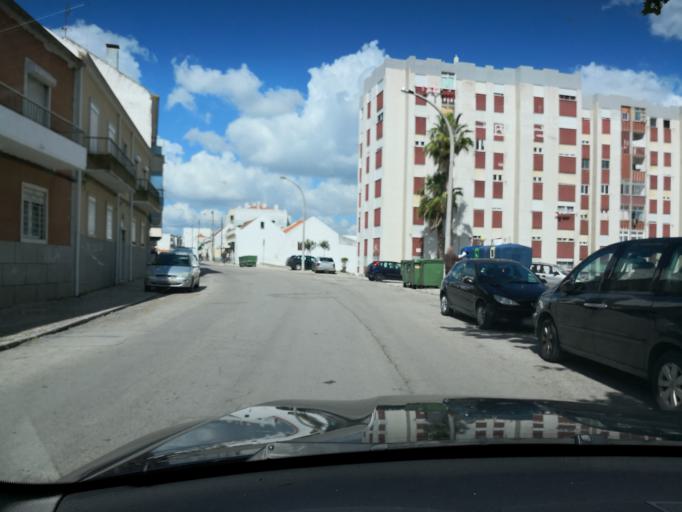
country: PT
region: Setubal
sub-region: Setubal
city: Setubal
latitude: 38.5244
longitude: -8.8708
